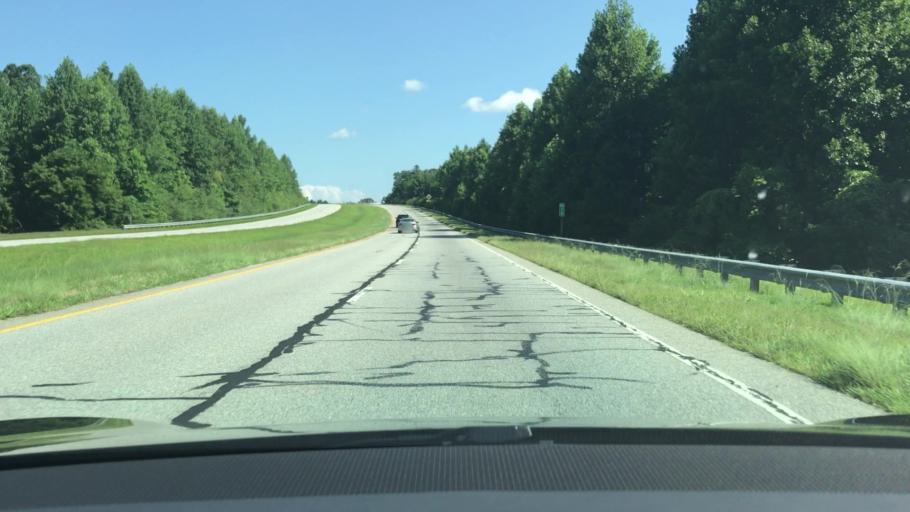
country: US
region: Georgia
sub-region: Habersham County
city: Clarkesville
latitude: 34.6209
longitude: -83.4471
